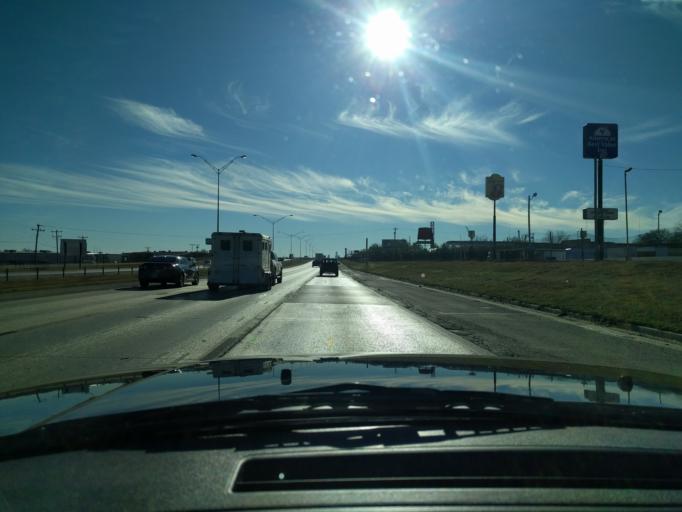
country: US
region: Oklahoma
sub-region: Oklahoma County
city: Edmond
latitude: 35.5887
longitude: -97.4369
